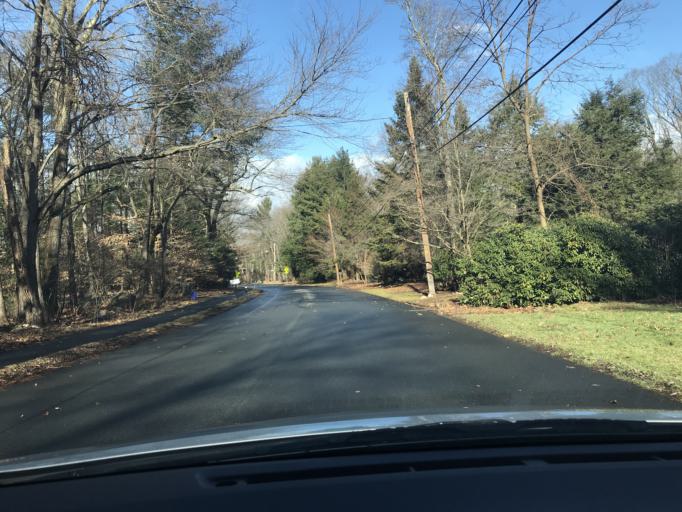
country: US
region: Massachusetts
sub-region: Middlesex County
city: Lexington
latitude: 42.4781
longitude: -71.2299
